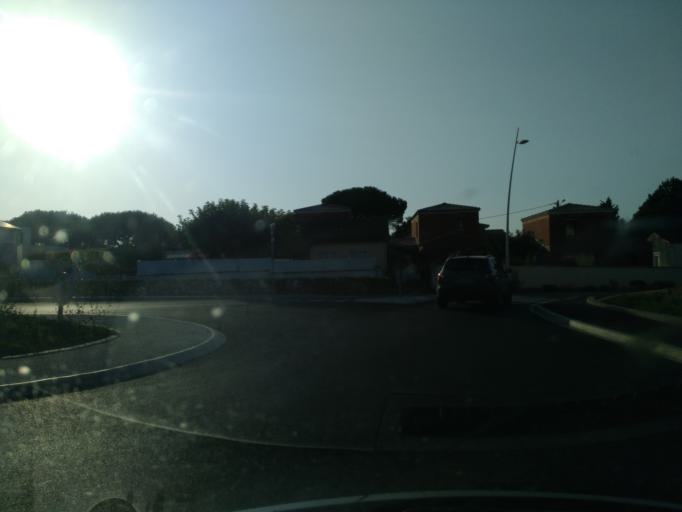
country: FR
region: Poitou-Charentes
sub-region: Departement de la Charente-Maritime
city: Vaux-sur-Mer
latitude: 45.6373
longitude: -1.0595
